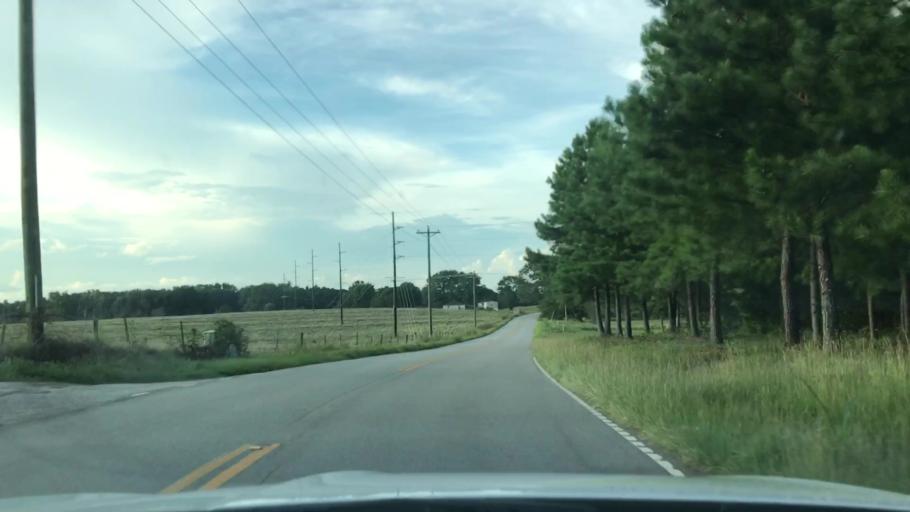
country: US
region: South Carolina
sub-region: Spartanburg County
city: Roebuck
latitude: 34.7877
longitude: -81.9170
